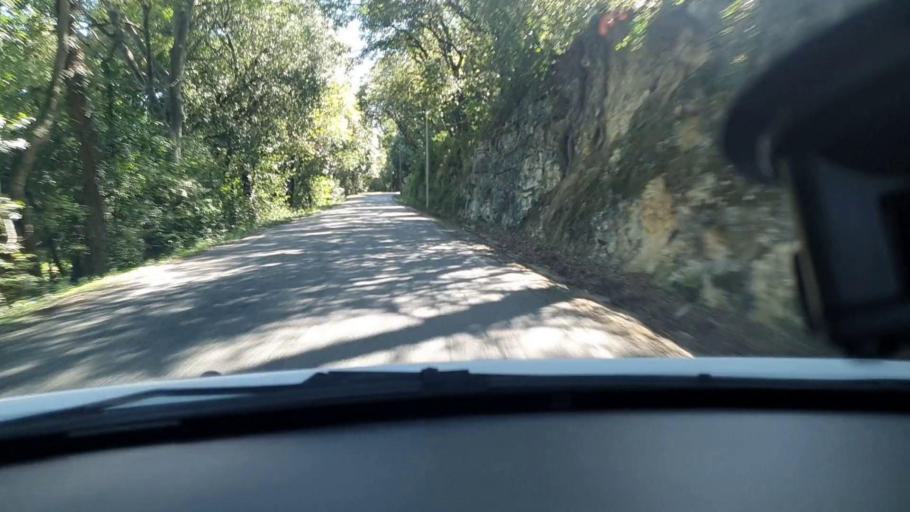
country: FR
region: Languedoc-Roussillon
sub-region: Departement du Gard
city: Sabran
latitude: 44.1917
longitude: 4.5219
